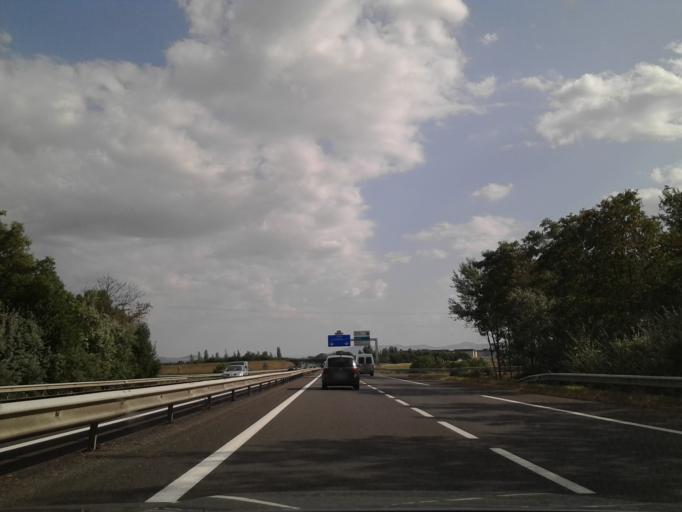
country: FR
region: Auvergne
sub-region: Departement du Puy-de-Dome
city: Riom
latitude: 45.9001
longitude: 3.1542
